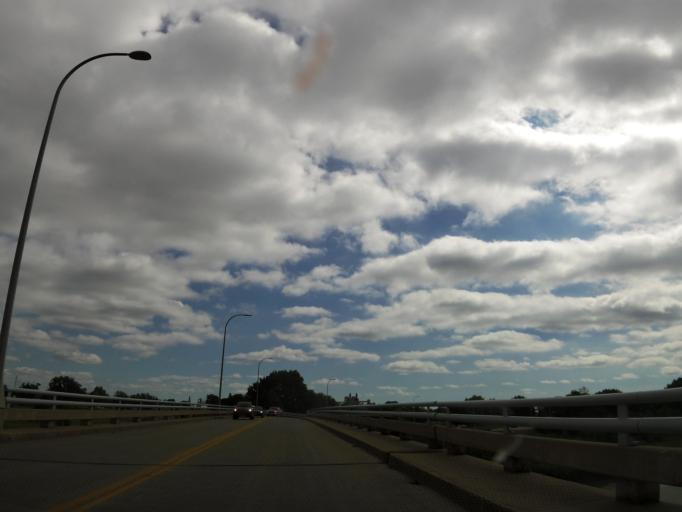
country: US
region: Minnesota
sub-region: Polk County
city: East Grand Forks
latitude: 47.9216
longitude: -97.0214
